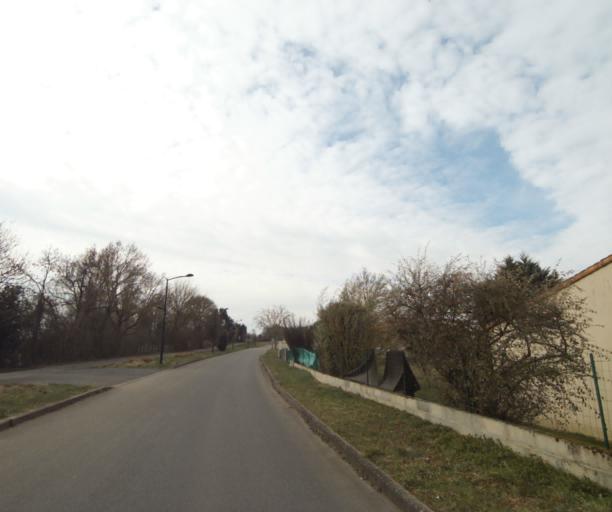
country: FR
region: Poitou-Charentes
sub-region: Departement des Deux-Sevres
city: Aiffres
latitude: 46.3142
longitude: -0.4295
